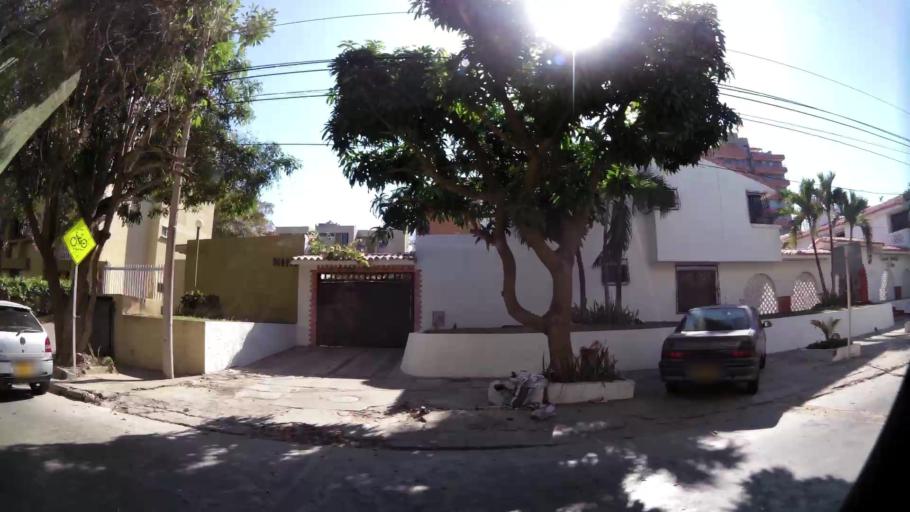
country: CO
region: Atlantico
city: Barranquilla
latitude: 11.0171
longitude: -74.8168
